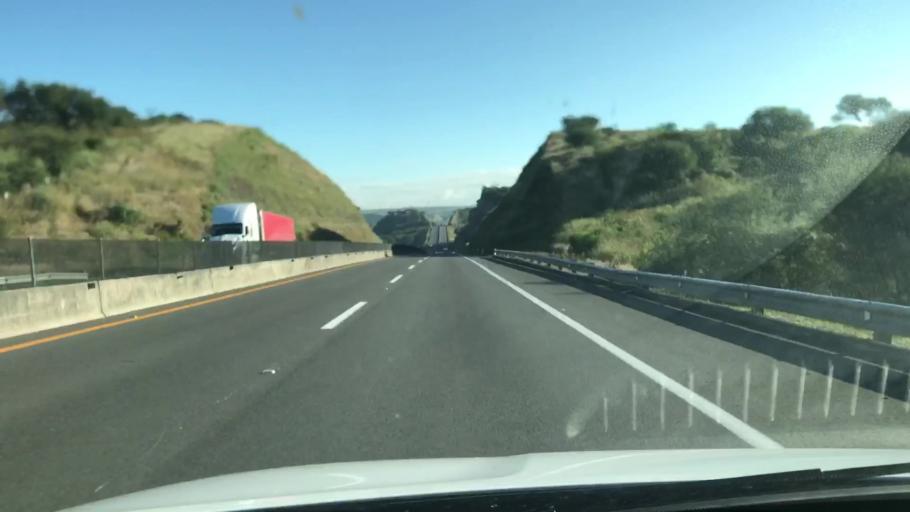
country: MX
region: Jalisco
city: Jalostotitlan
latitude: 21.1436
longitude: -102.4314
